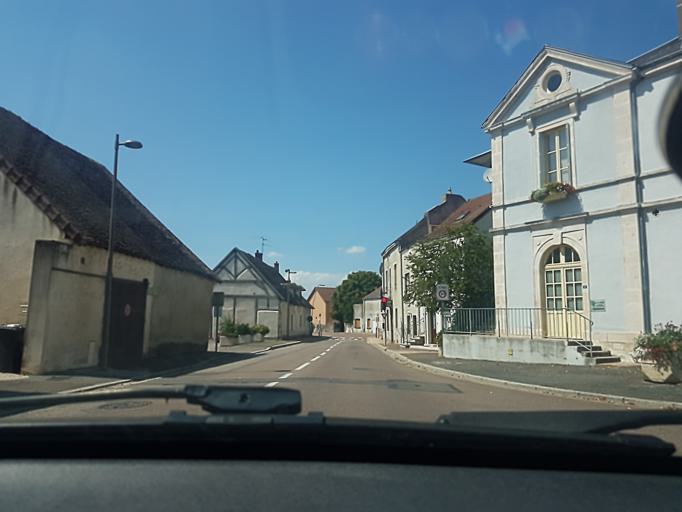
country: FR
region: Bourgogne
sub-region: Departement de Saone-et-Loire
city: Saint-Marcel
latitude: 46.7756
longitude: 4.8876
